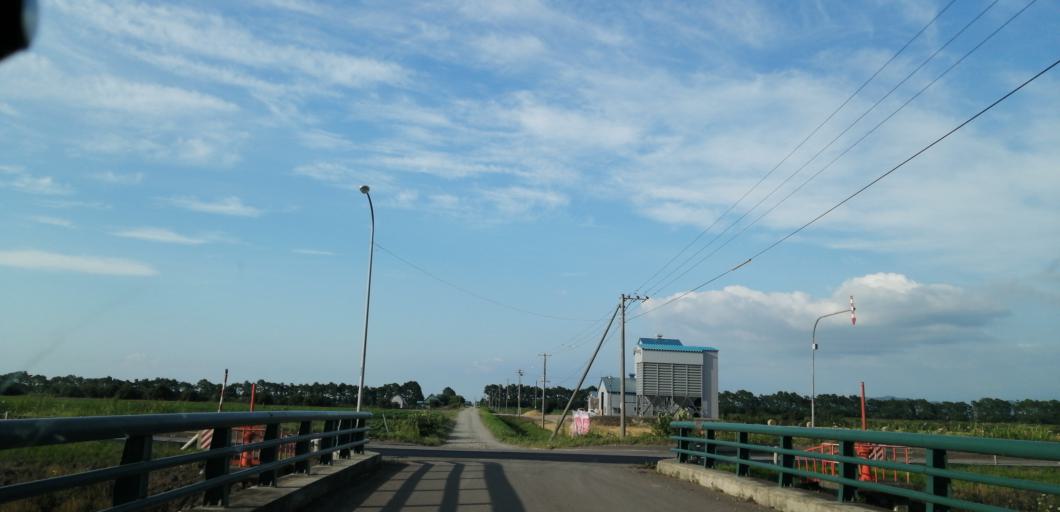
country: JP
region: Hokkaido
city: Kitahiroshima
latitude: 42.9736
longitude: 141.6524
